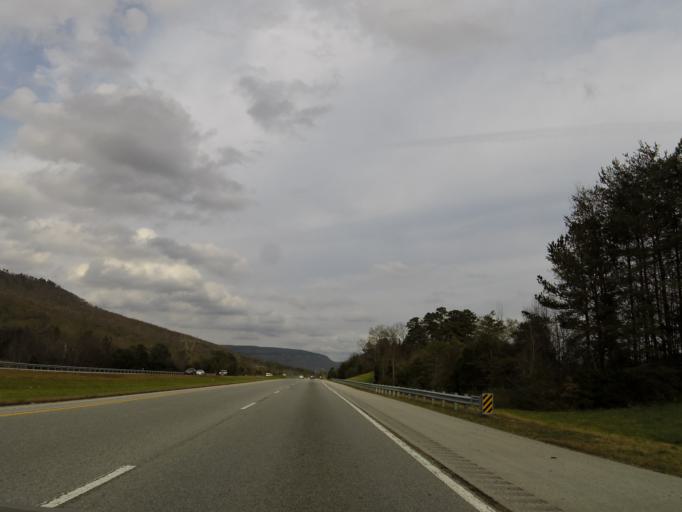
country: US
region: Tennessee
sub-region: Hamilton County
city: Walden
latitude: 35.1693
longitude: -85.2807
